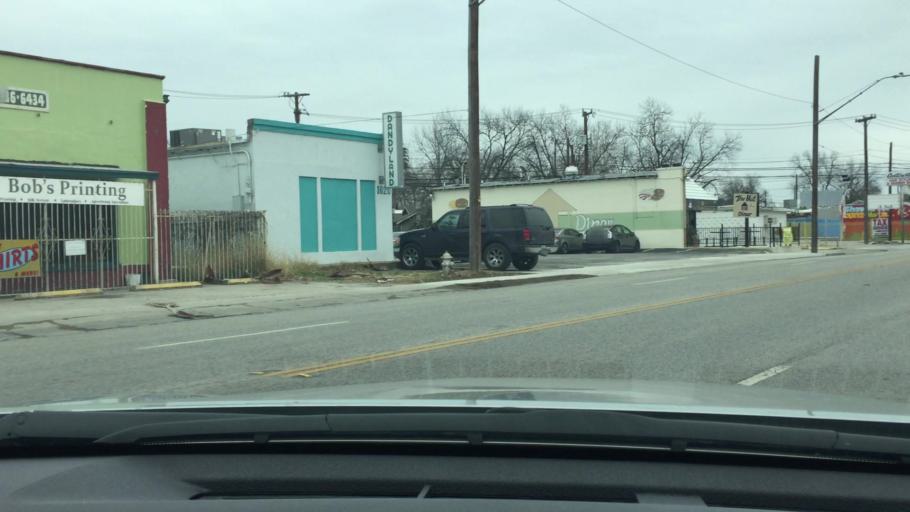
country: US
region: Texas
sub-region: Bexar County
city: Olmos Park
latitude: 29.4601
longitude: -98.5217
